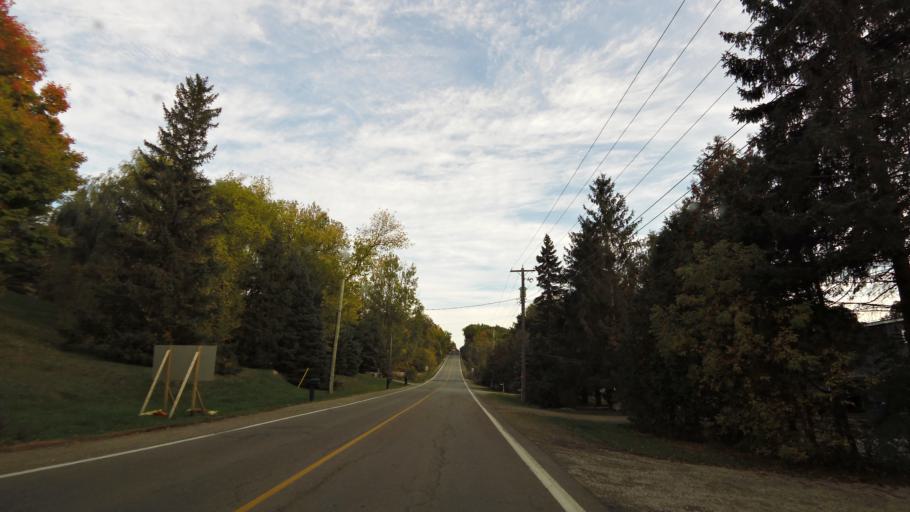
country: CA
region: Ontario
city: Brampton
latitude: 43.7087
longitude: -79.9345
